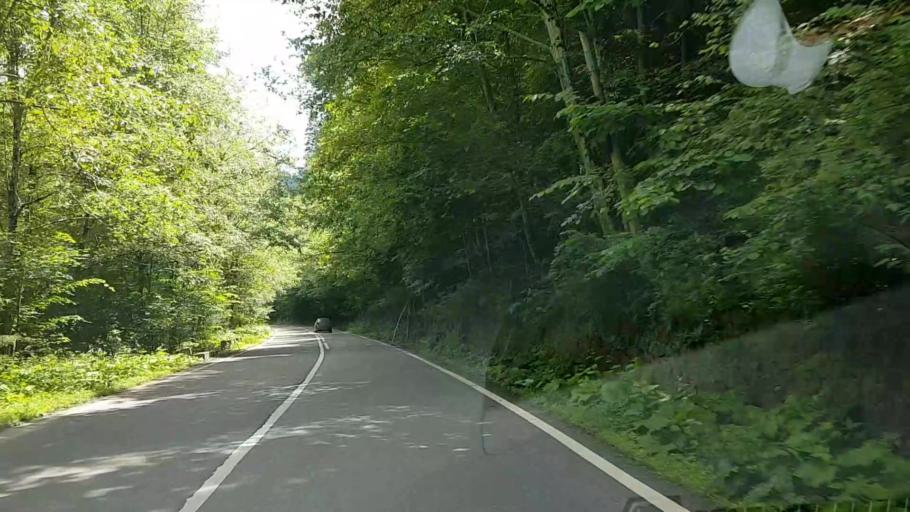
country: RO
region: Suceava
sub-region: Comuna Crucea
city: Crucea
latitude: 47.3090
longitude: 25.6226
